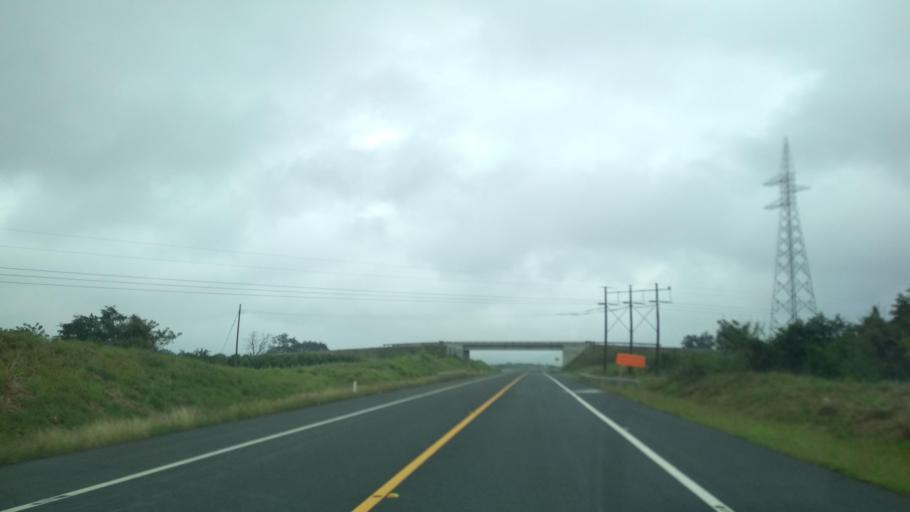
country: MX
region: Veracruz
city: Vega de San Marcos
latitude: 20.1554
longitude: -96.9514
